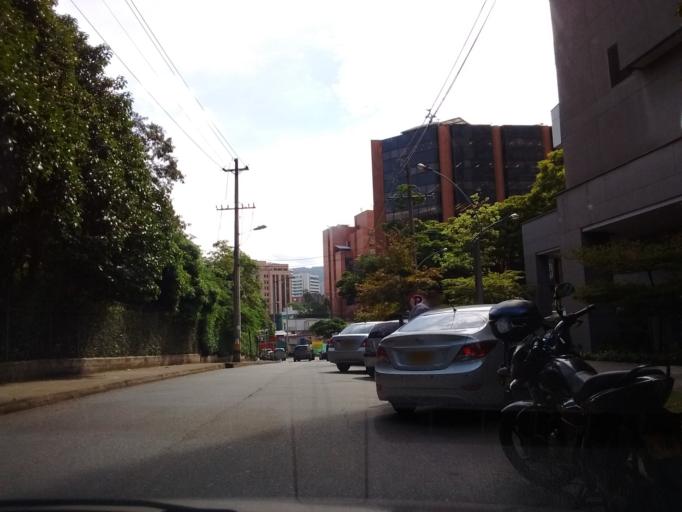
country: CO
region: Antioquia
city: Itagui
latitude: 6.2016
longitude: -75.5738
